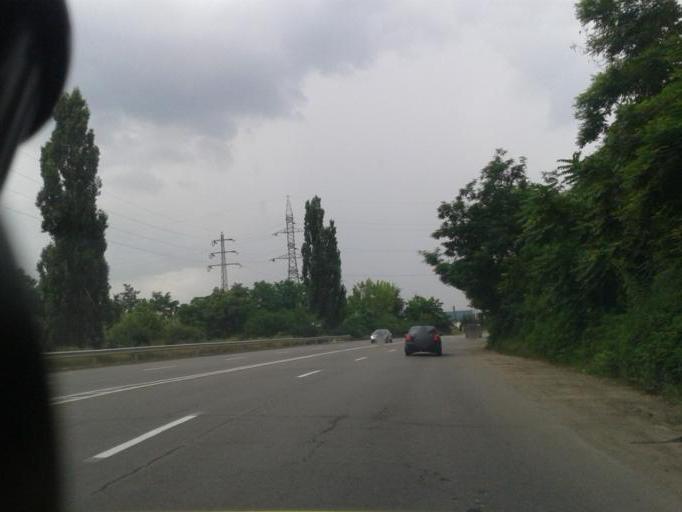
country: RO
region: Prahova
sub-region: Comuna Bucov
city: Bucov
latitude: 44.9630
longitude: 26.0603
